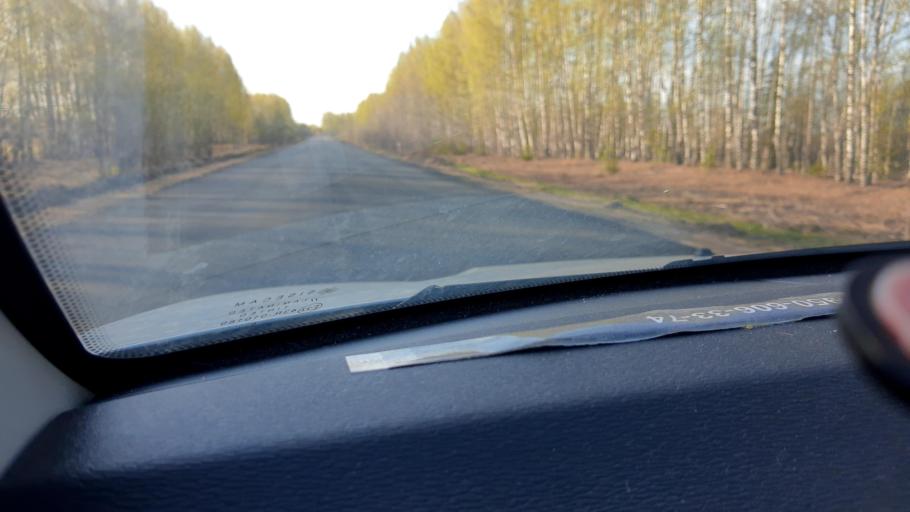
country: RU
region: Nizjnij Novgorod
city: Sharanga
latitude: 57.1212
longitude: 46.5195
